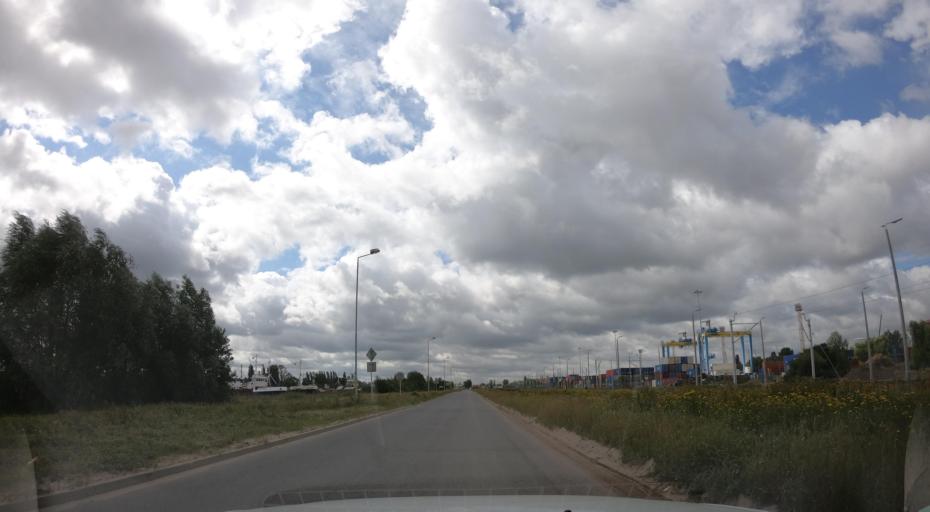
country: PL
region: West Pomeranian Voivodeship
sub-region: Szczecin
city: Szczecin
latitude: 53.4261
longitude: 14.5891
